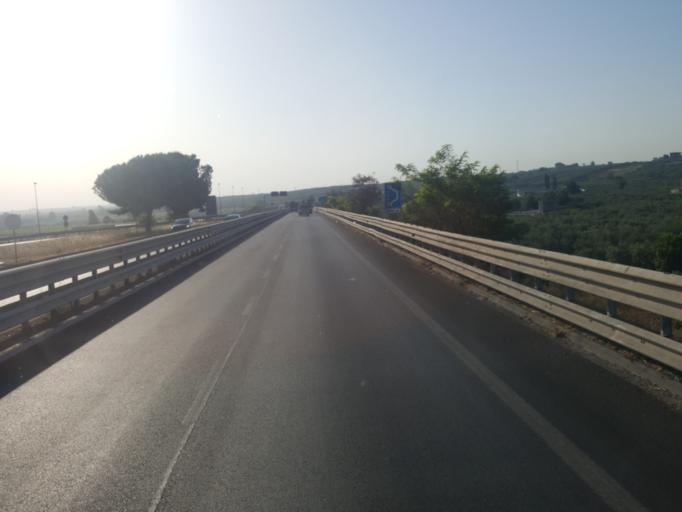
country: IT
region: Apulia
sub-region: Provincia di Foggia
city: Cerignola
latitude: 41.2808
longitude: 15.8963
